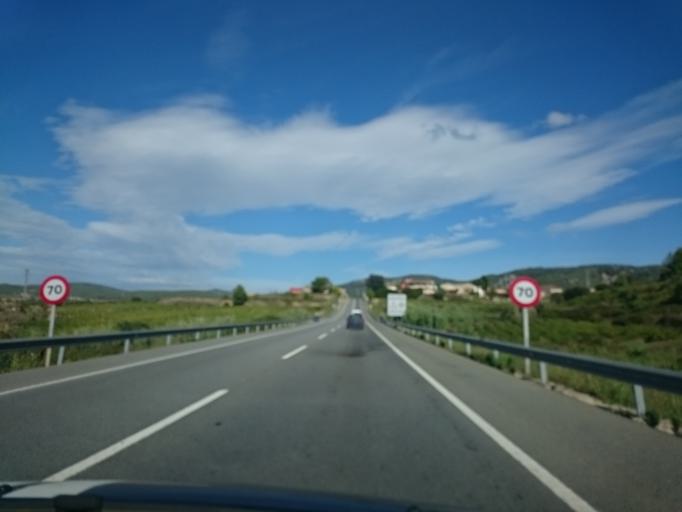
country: ES
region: Catalonia
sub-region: Provincia de Barcelona
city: Avinyonet del Penedes
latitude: 41.3662
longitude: 1.7945
